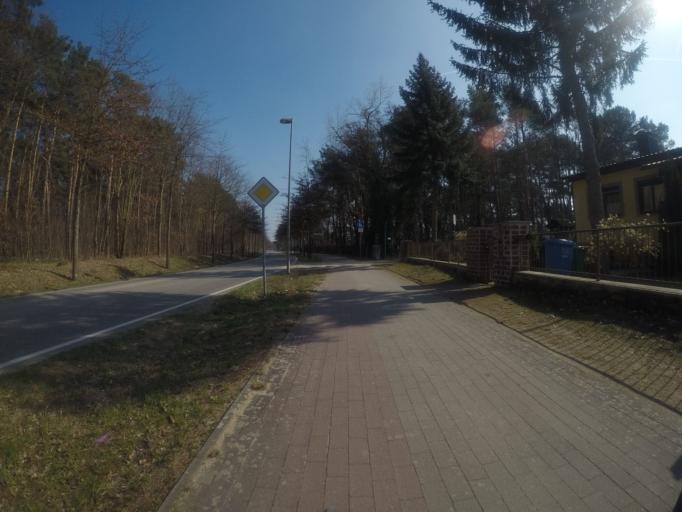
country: DE
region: Brandenburg
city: Konigs Wusterhausen
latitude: 52.2993
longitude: 13.7127
